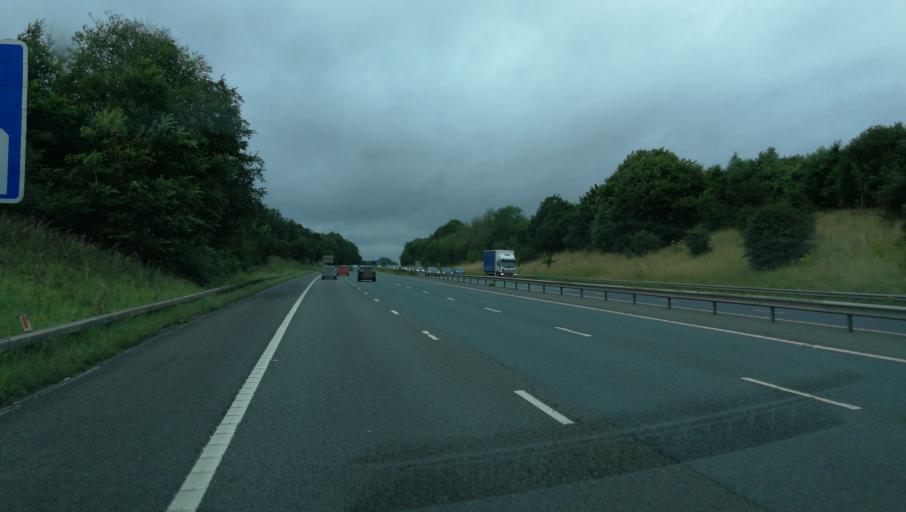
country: GB
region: England
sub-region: Borough of Wigan
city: Atherton
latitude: 53.5496
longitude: -2.4724
